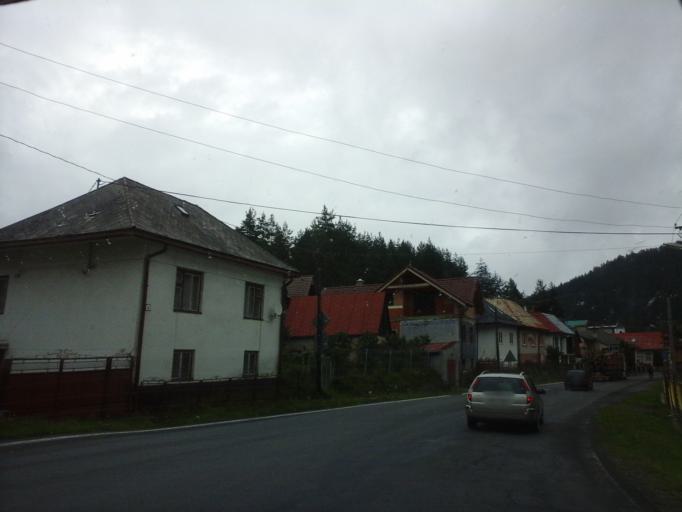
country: SK
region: Kosicky
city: Dobsina
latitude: 48.9170
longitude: 20.2651
